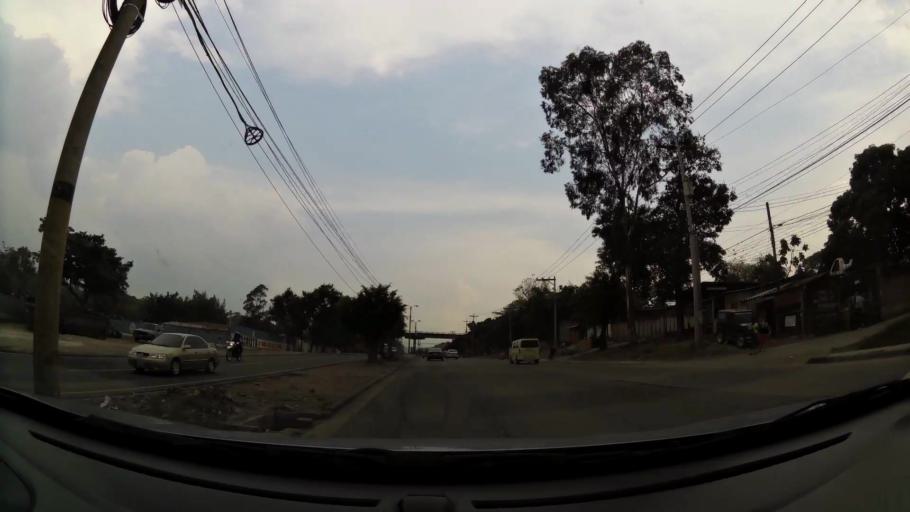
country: HN
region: Francisco Morazan
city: Tegucigalpa
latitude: 14.0812
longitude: -87.2176
